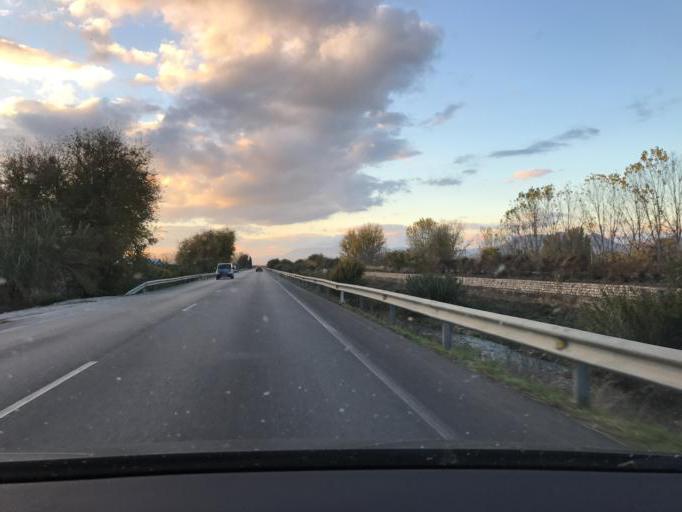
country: ES
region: Andalusia
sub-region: Provincia de Granada
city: Churriana de la Vega
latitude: 37.1657
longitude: -3.6354
